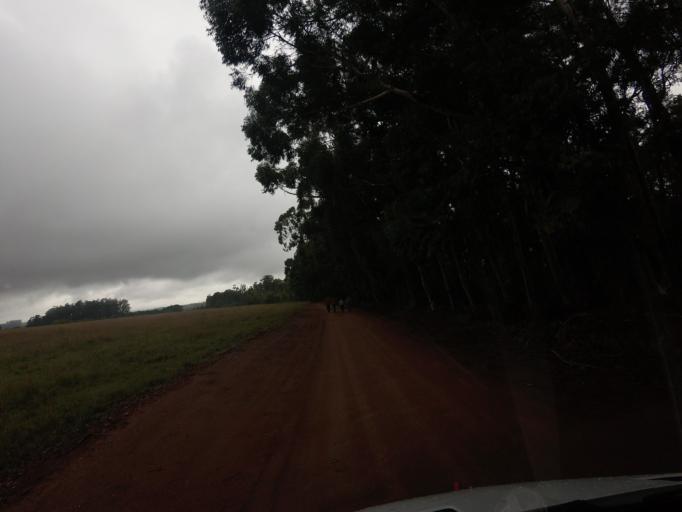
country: SZ
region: Hhohho
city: Lobamba
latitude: -26.4803
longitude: 31.1857
